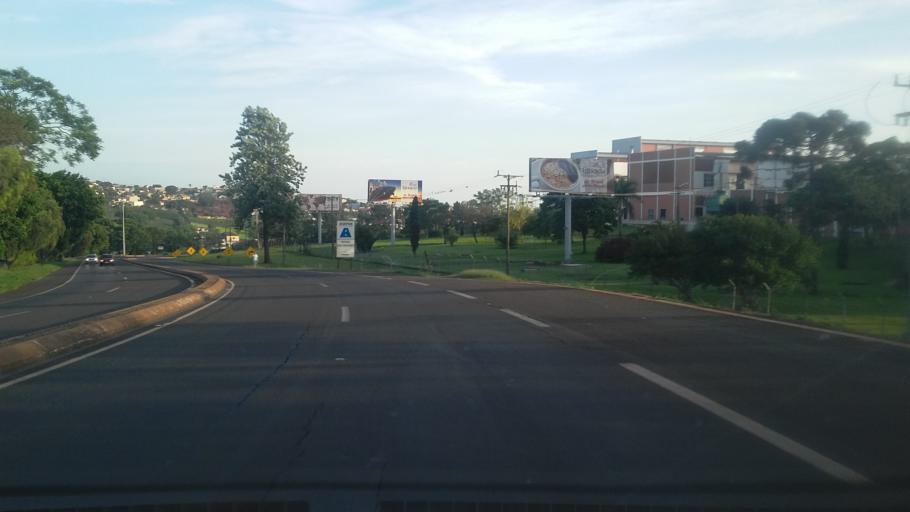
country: BR
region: Parana
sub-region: Assai
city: Assai
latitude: -23.1873
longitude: -50.6391
